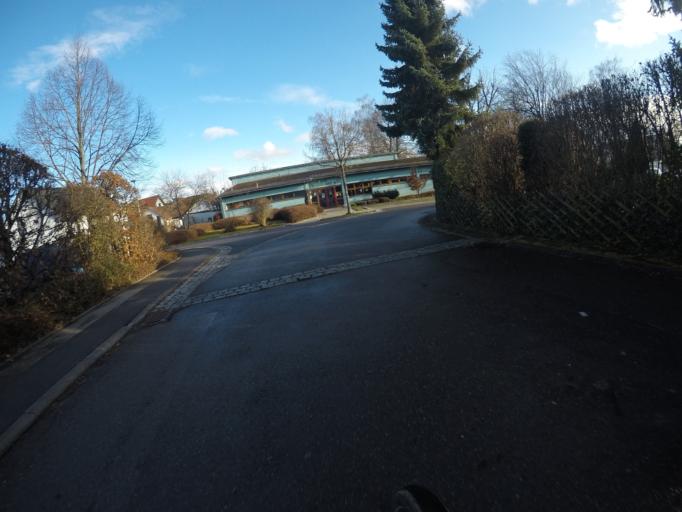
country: DE
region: Baden-Wuerttemberg
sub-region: Regierungsbezirk Stuttgart
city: Herrenberg
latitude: 48.5646
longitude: 8.8475
